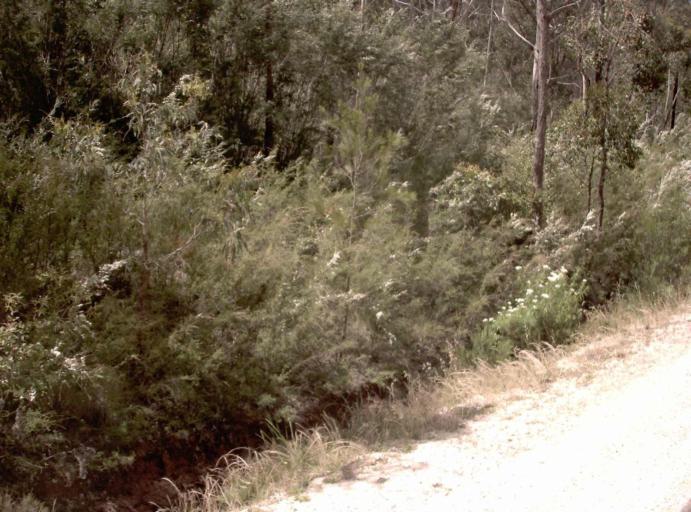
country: AU
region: New South Wales
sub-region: Bombala
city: Bombala
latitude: -37.5456
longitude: 149.4376
